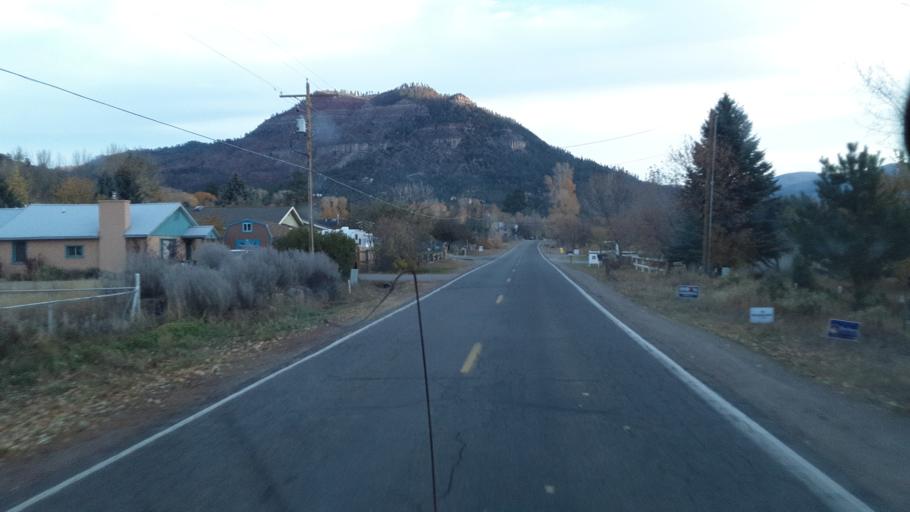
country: US
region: Colorado
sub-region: La Plata County
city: Durango
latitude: 37.4085
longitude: -107.8426
